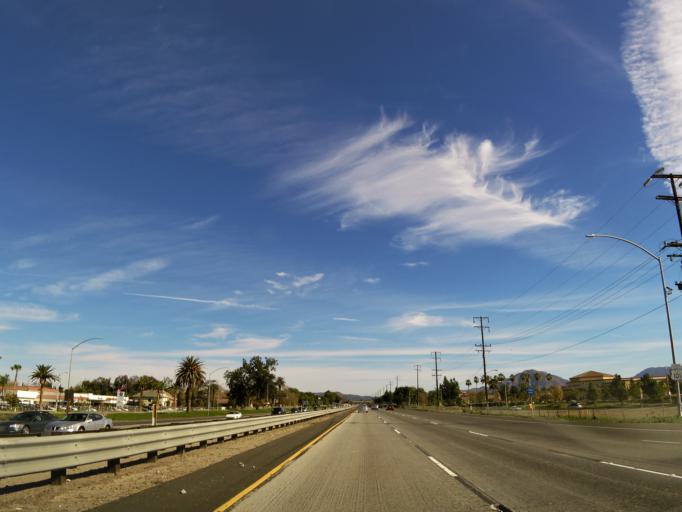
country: US
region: California
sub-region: Ventura County
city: Camarillo
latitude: 34.2187
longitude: -119.0665
